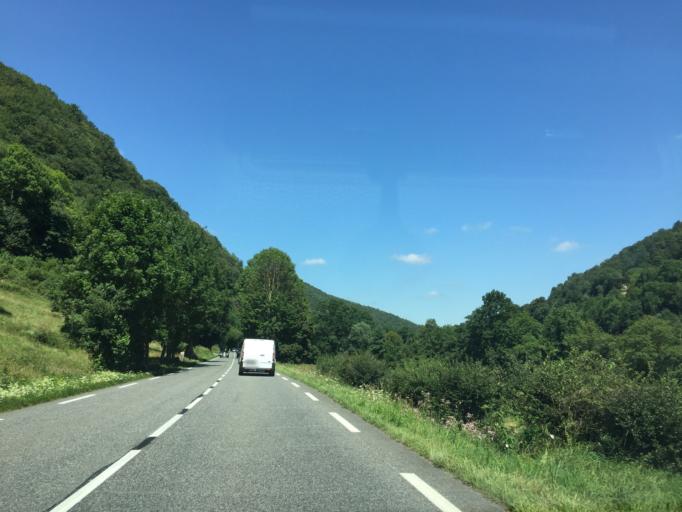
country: FR
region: Midi-Pyrenees
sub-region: Departement des Hautes-Pyrenees
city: La Barthe-de-Neste
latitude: 42.9862
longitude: 0.3759
